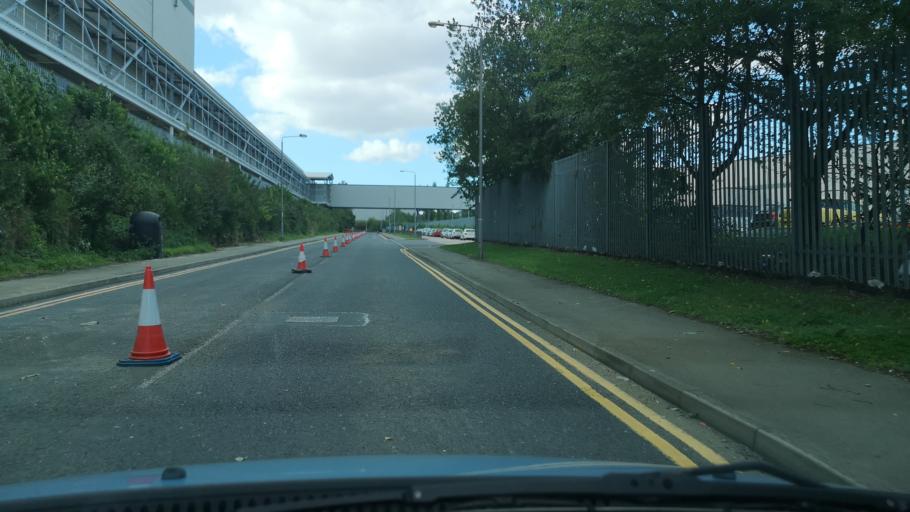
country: GB
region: England
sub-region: City and Borough of Wakefield
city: South Elmsall
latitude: 53.6017
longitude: -1.2692
